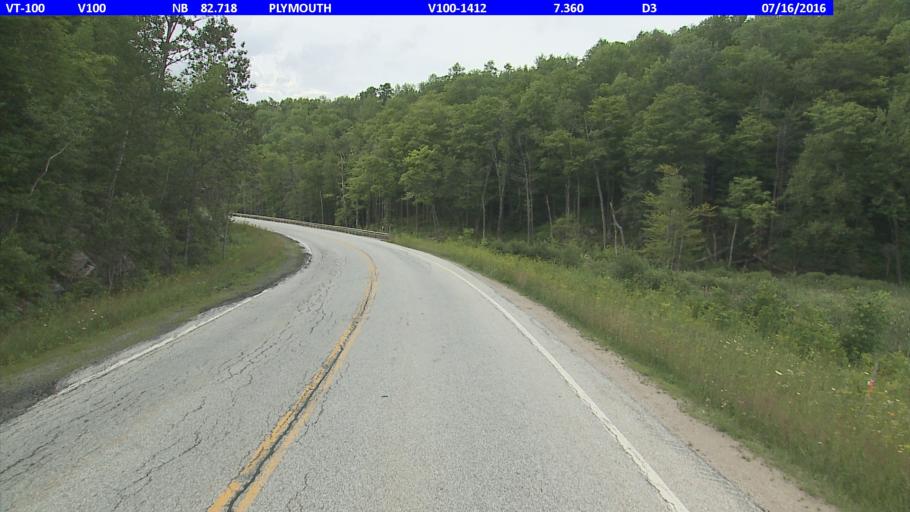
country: US
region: Vermont
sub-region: Rutland County
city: Rutland
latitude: 43.5557
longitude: -72.7568
